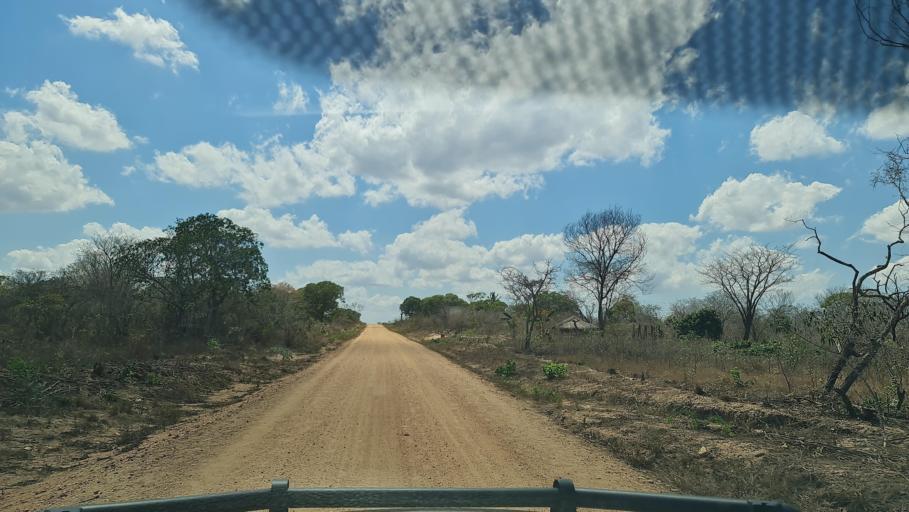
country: MZ
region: Nampula
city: Nacala
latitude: -14.1766
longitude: 40.2279
